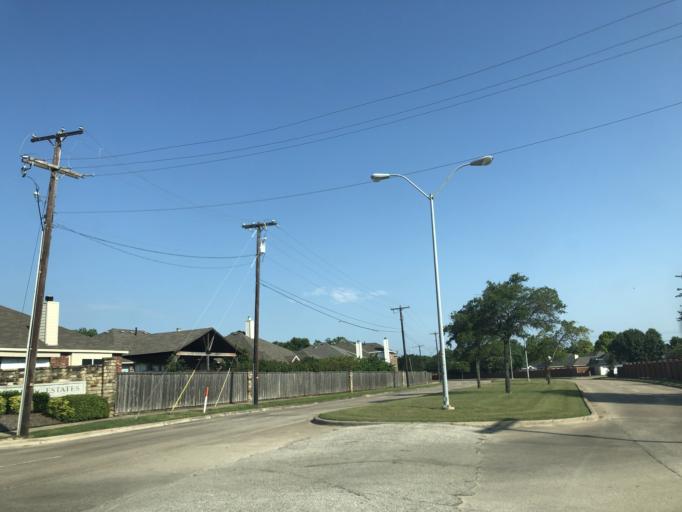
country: US
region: Texas
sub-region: Dallas County
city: Sunnyvale
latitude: 32.8294
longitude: -96.5980
